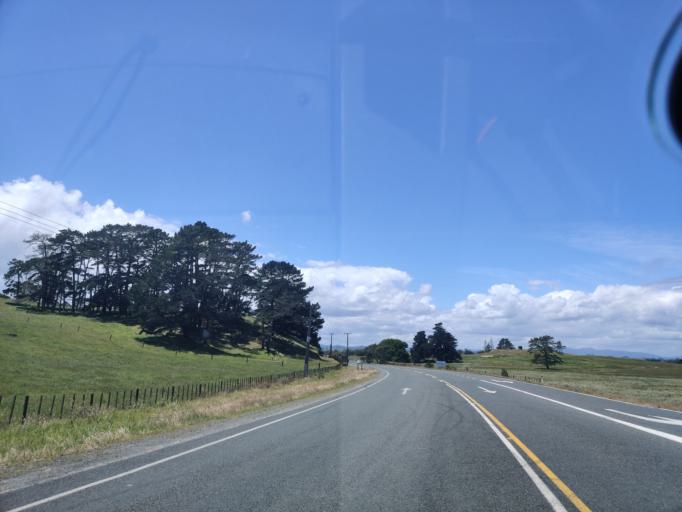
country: NZ
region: Northland
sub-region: Far North District
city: Kaitaia
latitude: -35.0212
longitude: 173.2171
